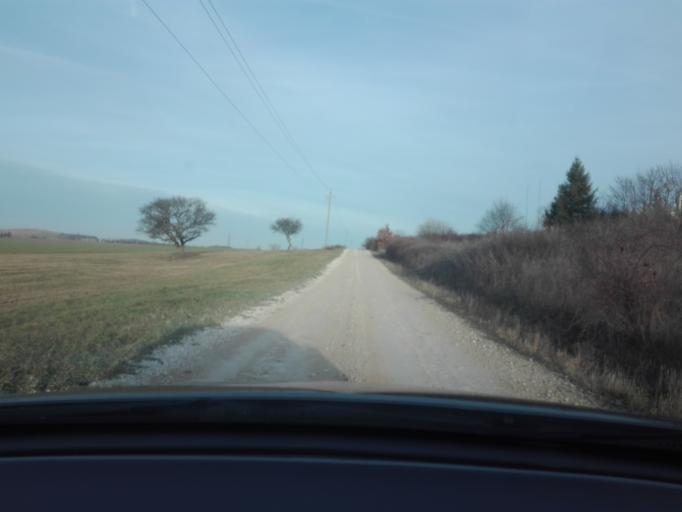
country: HU
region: Veszprem
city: Nemesvamos
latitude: 47.0152
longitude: 17.7916
